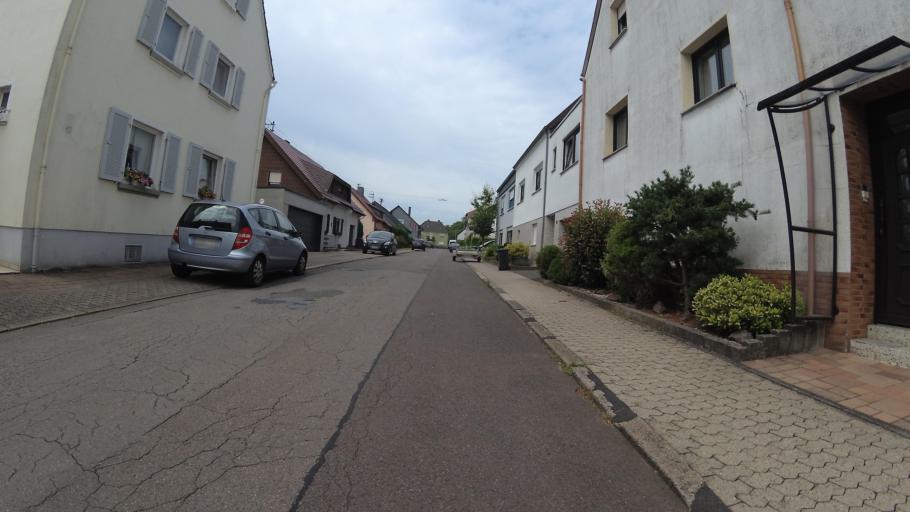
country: DE
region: Saarland
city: Quierschied
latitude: 49.3243
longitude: 7.0467
